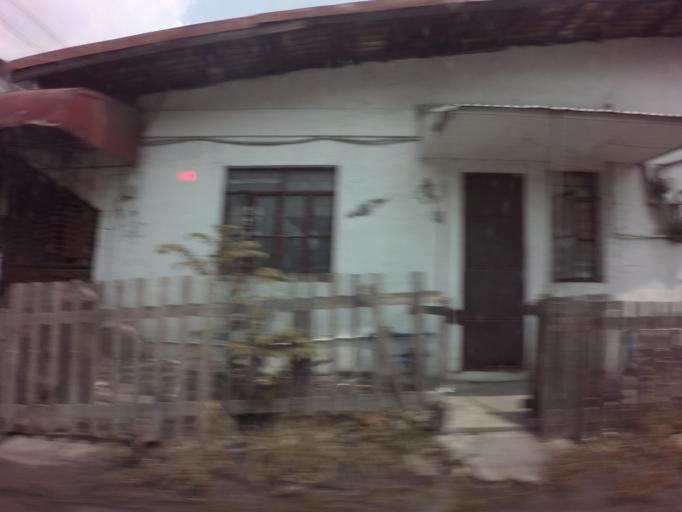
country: PH
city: Sambayanihan People's Village
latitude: 14.4376
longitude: 121.0502
